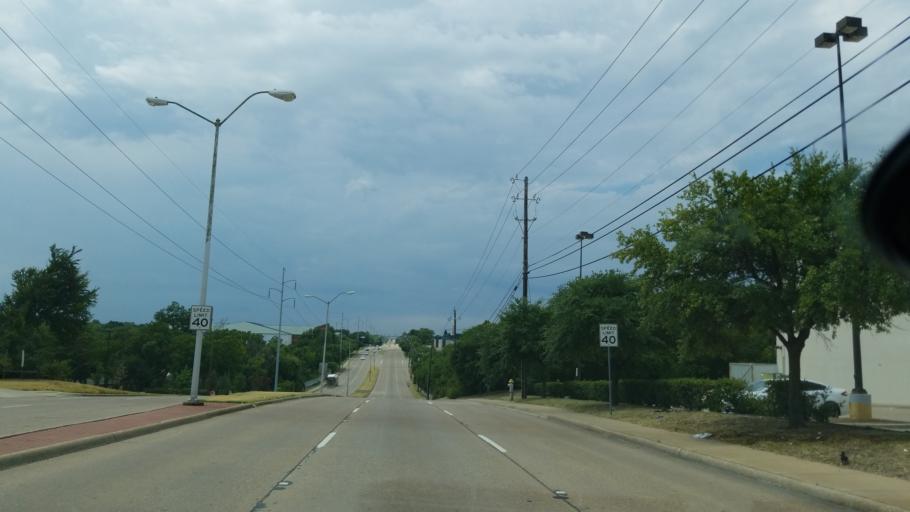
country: US
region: Texas
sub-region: Dallas County
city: Duncanville
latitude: 32.6622
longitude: -96.8429
